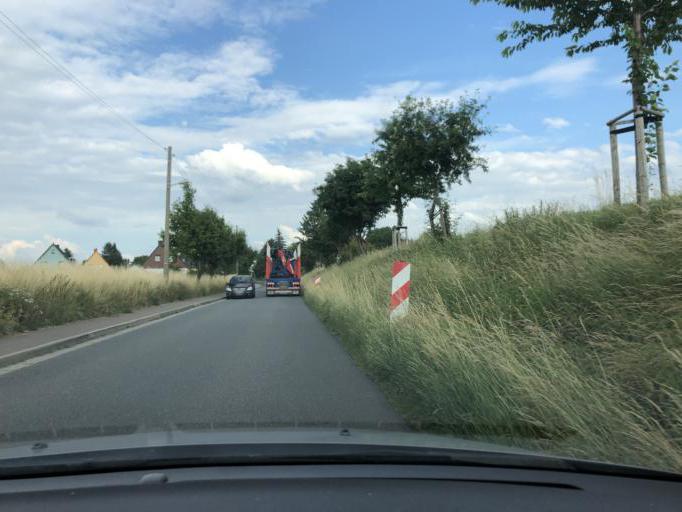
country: DE
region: Saxony
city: Freital
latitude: 51.0445
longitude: 13.6158
